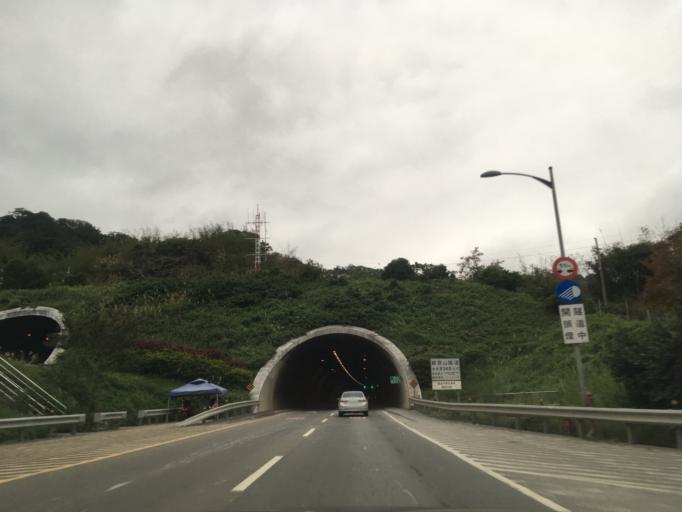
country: TW
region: Taipei
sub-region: Taipei
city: Banqiao
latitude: 25.1117
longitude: 121.4219
